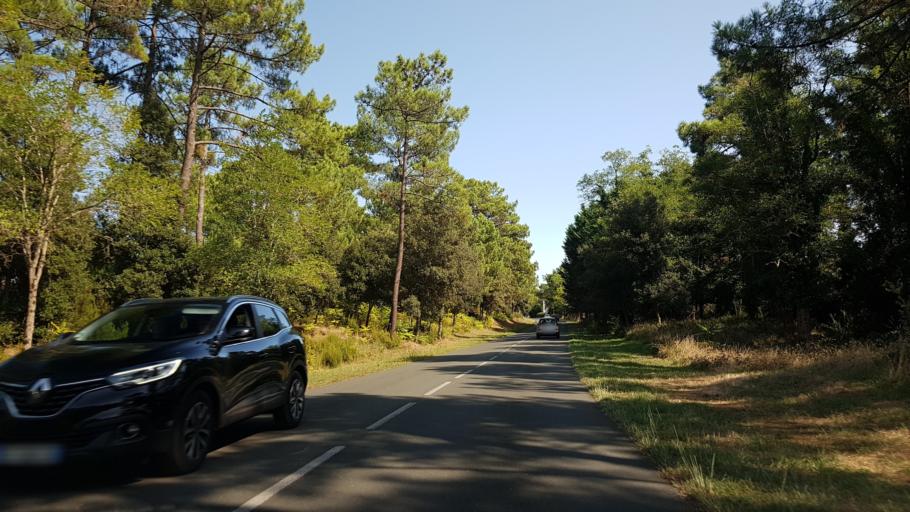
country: FR
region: Poitou-Charentes
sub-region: Departement de la Charente-Maritime
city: Les Mathes
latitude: 45.6993
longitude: -1.2060
